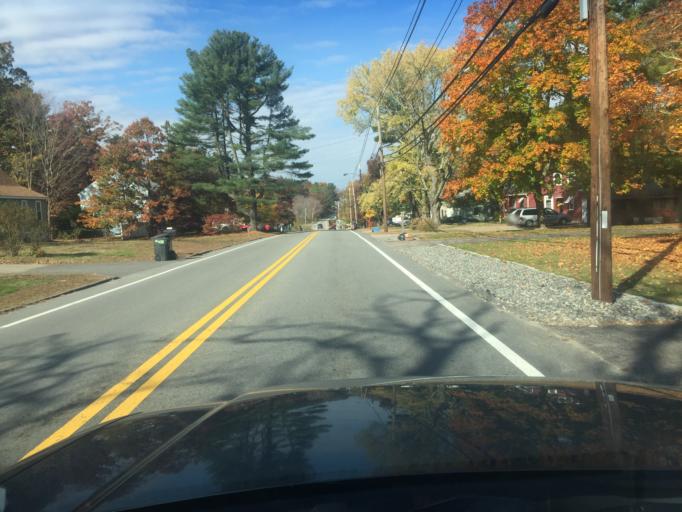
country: US
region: Massachusetts
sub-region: Worcester County
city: Milford
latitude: 42.1145
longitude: -71.5101
